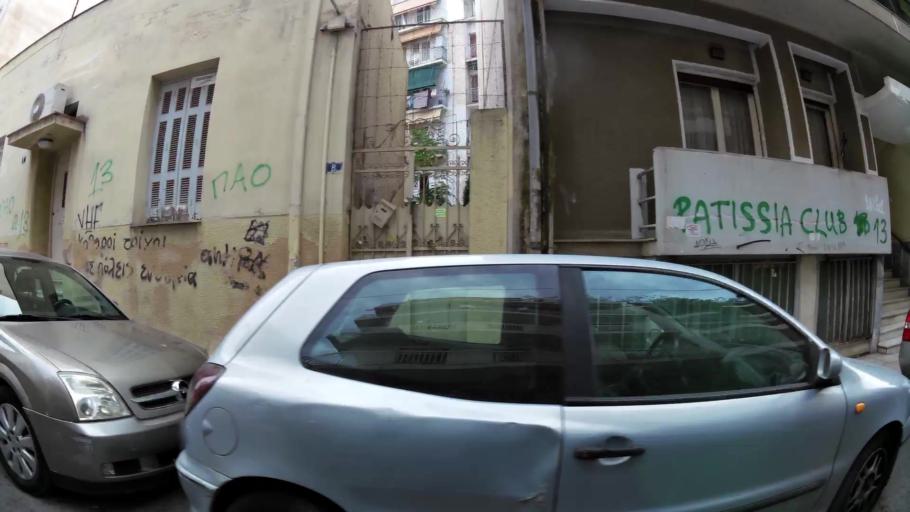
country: GR
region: Attica
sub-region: Nomarchia Athinas
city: Kipseli
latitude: 38.0034
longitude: 23.7243
